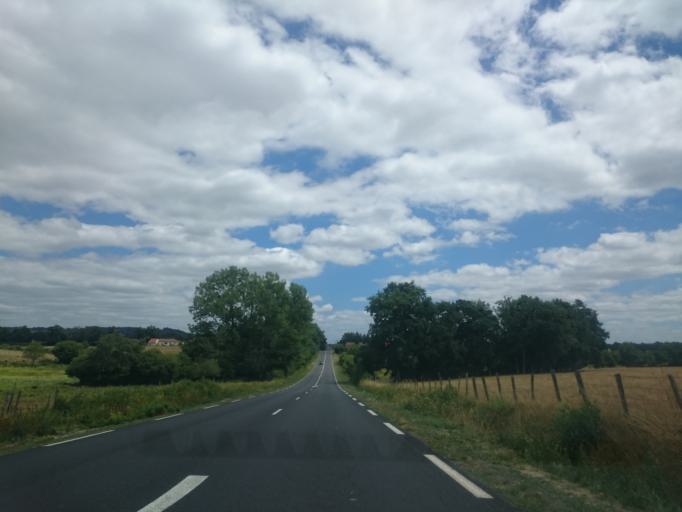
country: FR
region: Auvergne
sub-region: Departement du Cantal
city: Saint-Paul-des-Landes
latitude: 44.9497
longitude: 2.2963
